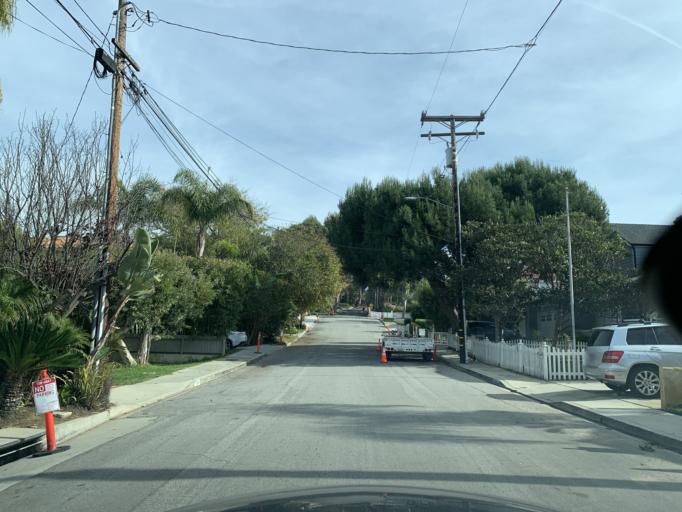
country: US
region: California
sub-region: Los Angeles County
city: Manhattan Beach
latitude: 33.8819
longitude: -118.3947
